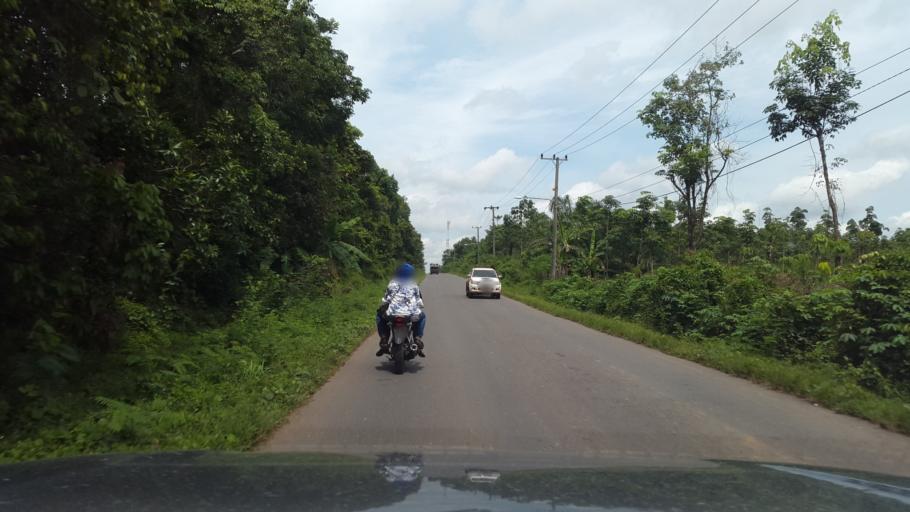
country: ID
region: South Sumatra
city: Gunungmegang Dalam
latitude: -3.3928
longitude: 103.9578
